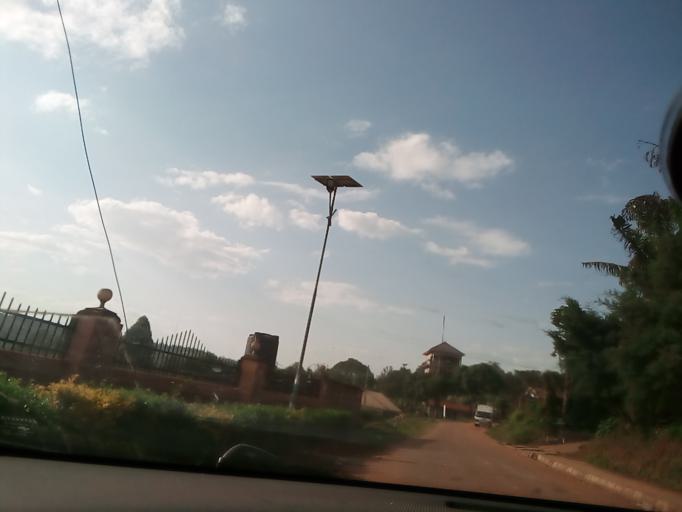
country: UG
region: Central Region
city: Masaka
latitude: -0.3542
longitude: 31.7441
